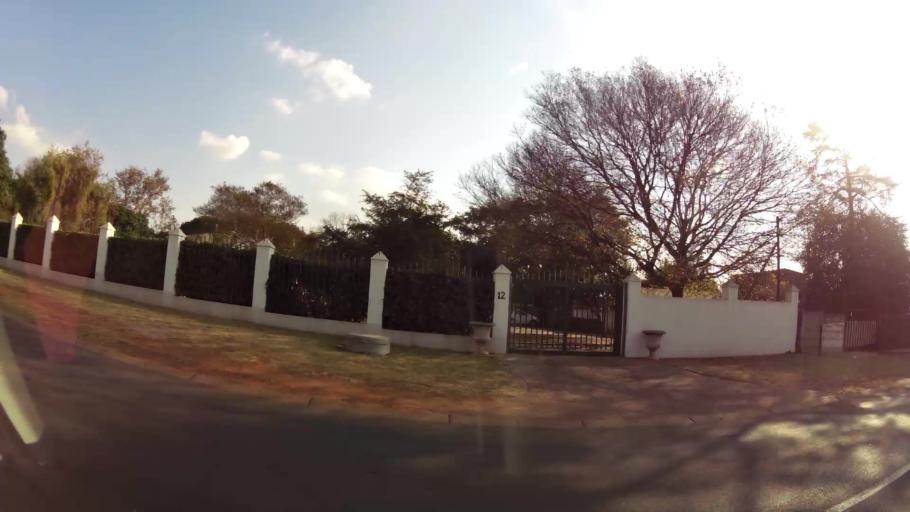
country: ZA
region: Gauteng
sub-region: Ekurhuleni Metropolitan Municipality
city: Tembisa
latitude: -25.9541
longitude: 28.2296
